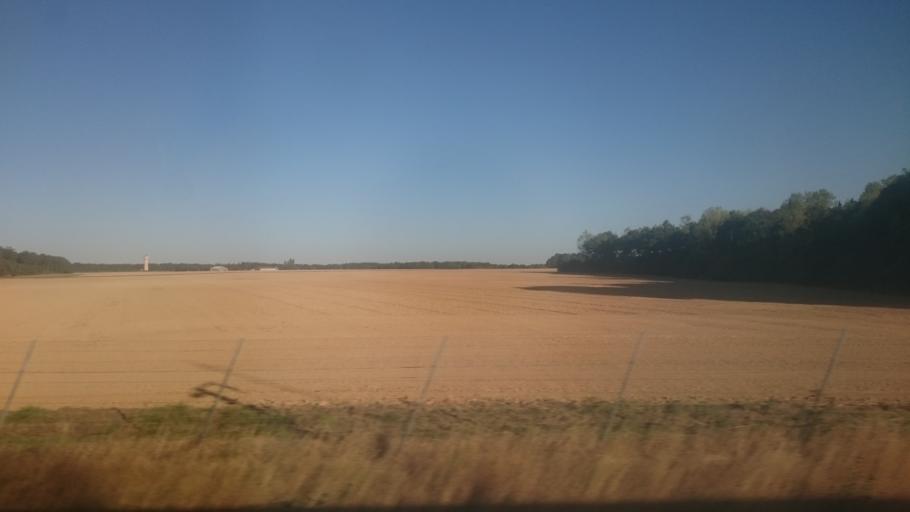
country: FR
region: Centre
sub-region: Departement d'Eure-et-Loir
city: Marboue
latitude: 48.1734
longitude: 1.2856
